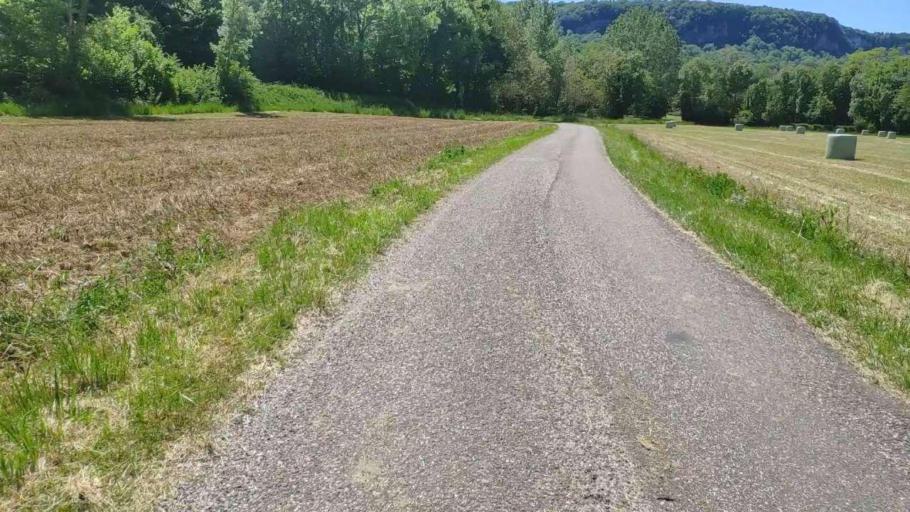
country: FR
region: Franche-Comte
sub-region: Departement du Jura
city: Perrigny
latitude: 46.7340
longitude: 5.6454
